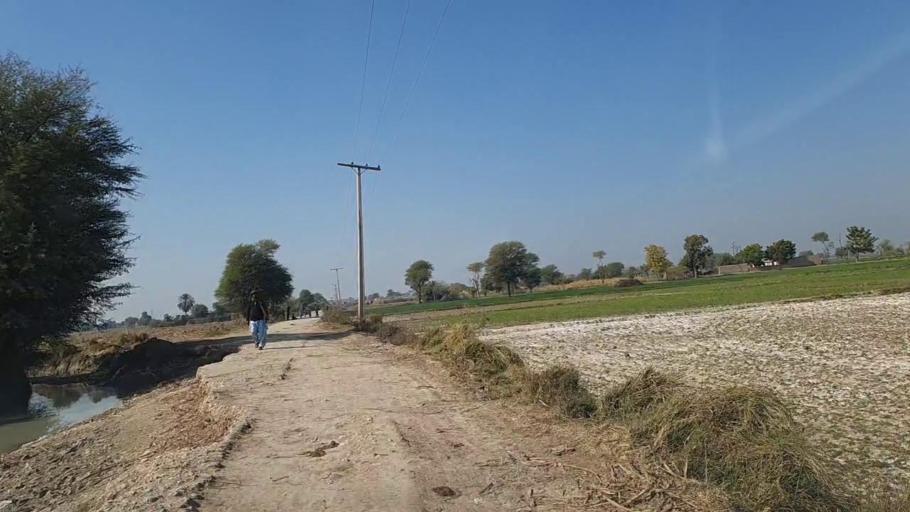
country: PK
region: Sindh
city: Nawabshah
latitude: 26.2870
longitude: 68.3781
